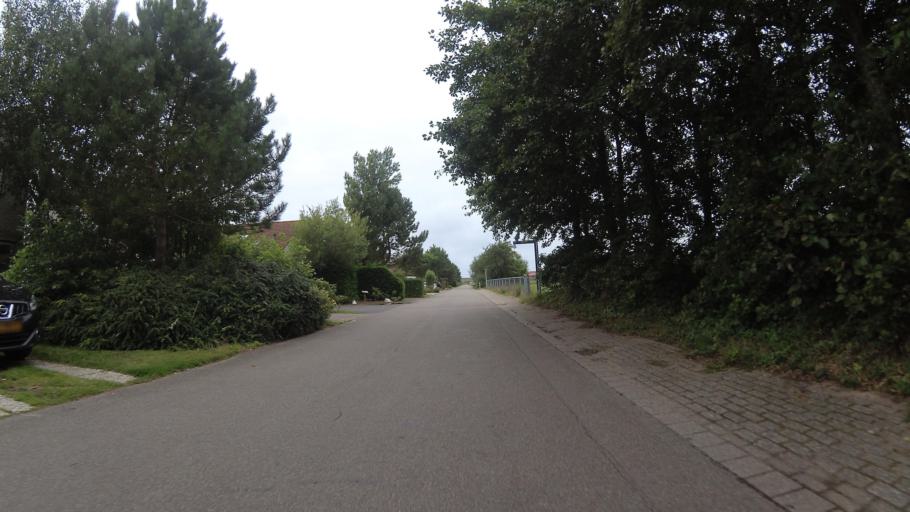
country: NL
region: North Holland
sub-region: Gemeente Den Helder
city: Den Helder
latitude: 52.8897
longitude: 4.7282
